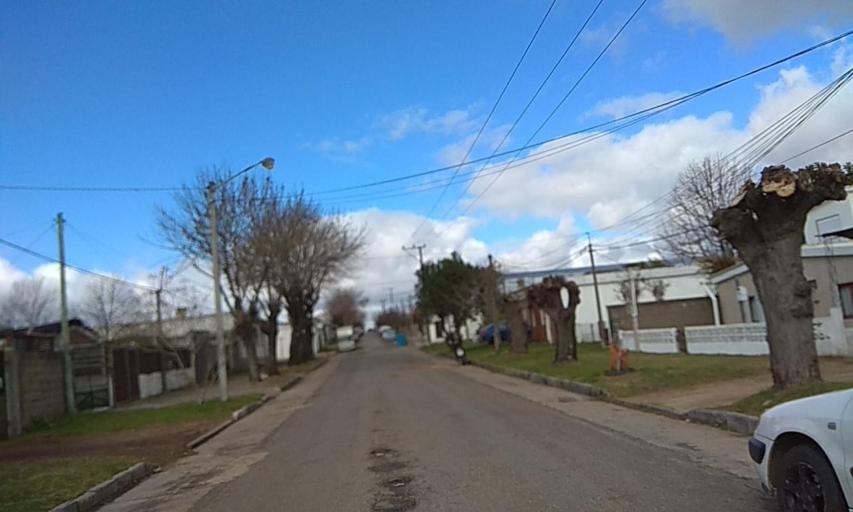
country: UY
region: Florida
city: Florida
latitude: -34.1006
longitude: -56.2223
